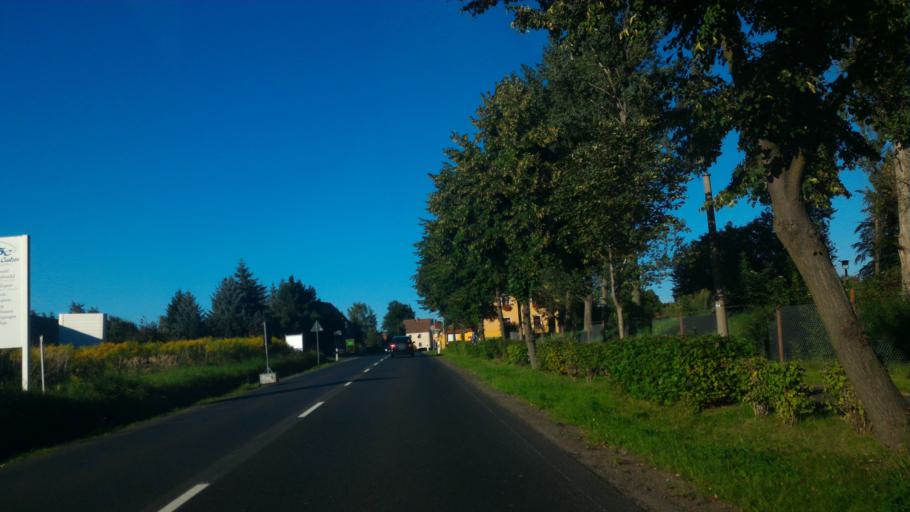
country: DE
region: Saxony
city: Hirschfelde
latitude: 50.9409
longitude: 14.8812
